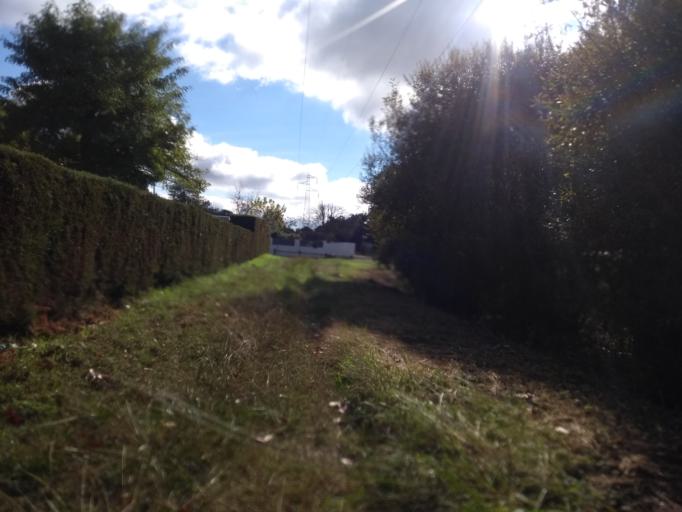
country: FR
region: Aquitaine
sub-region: Departement de la Gironde
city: Canejan
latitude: 44.7702
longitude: -0.6500
